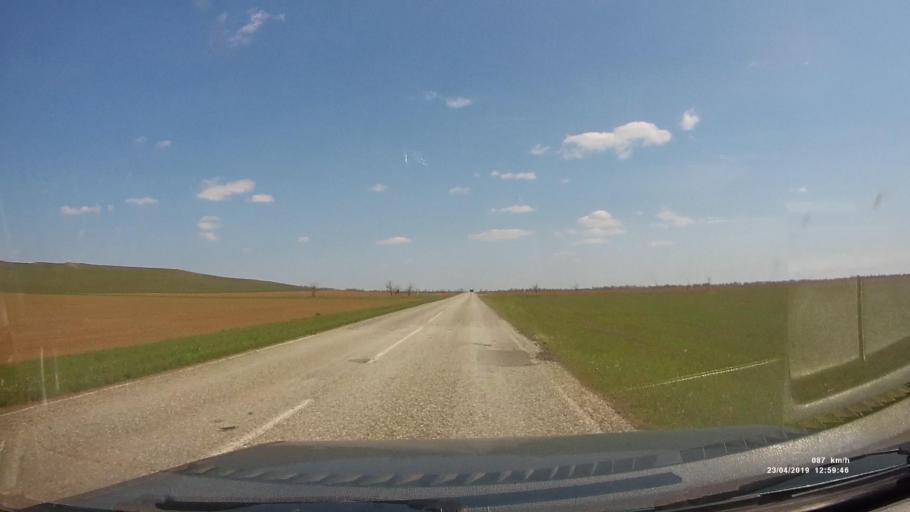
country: RU
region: Kalmykiya
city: Yashalta
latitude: 46.6042
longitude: 42.6219
